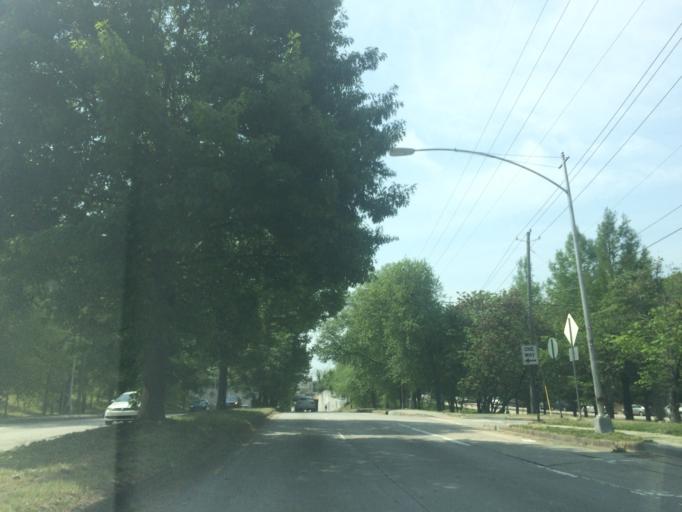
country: US
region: Georgia
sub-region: DeKalb County
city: Druid Hills
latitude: 33.7622
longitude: -84.3493
